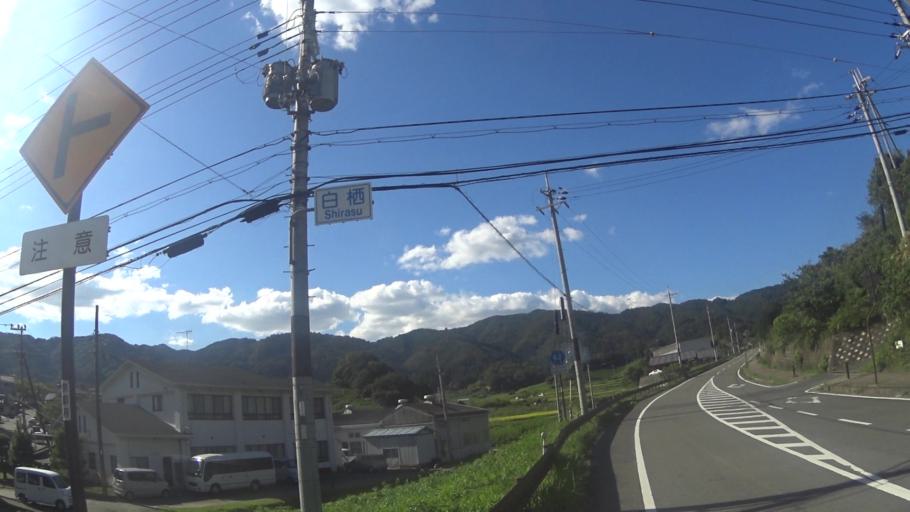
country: JP
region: Kyoto
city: Uji
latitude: 34.7961
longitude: 135.8987
